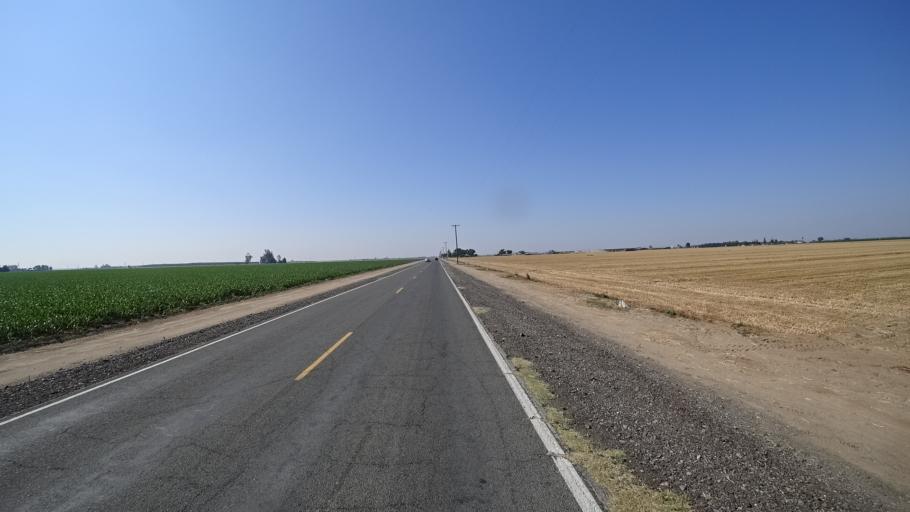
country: US
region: California
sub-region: Kings County
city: Hanford
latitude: 36.3791
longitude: -119.5650
